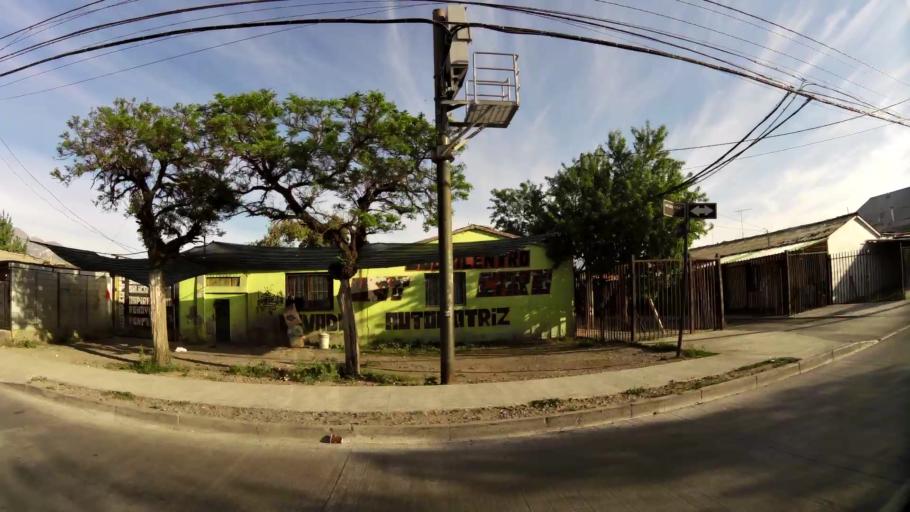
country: CL
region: Santiago Metropolitan
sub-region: Provincia de Cordillera
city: Puente Alto
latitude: -33.6142
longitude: -70.5780
